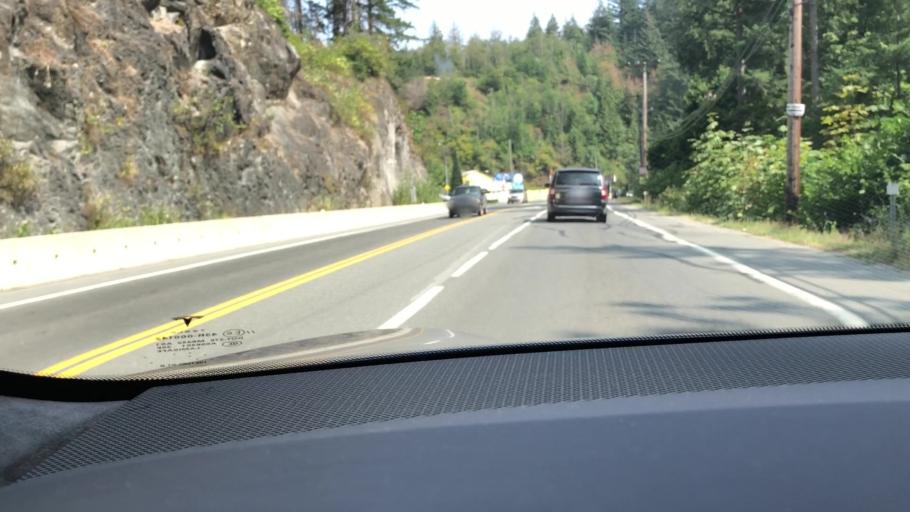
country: CA
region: British Columbia
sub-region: Fraser Valley Regional District
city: Chilliwack
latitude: 49.0922
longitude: -121.9698
